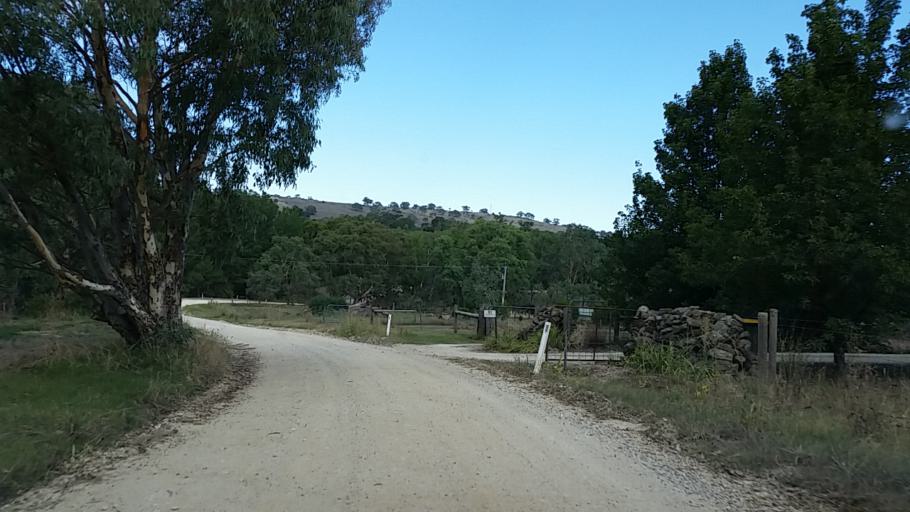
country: AU
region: South Australia
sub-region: Barossa
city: Angaston
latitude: -34.5644
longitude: 139.0794
